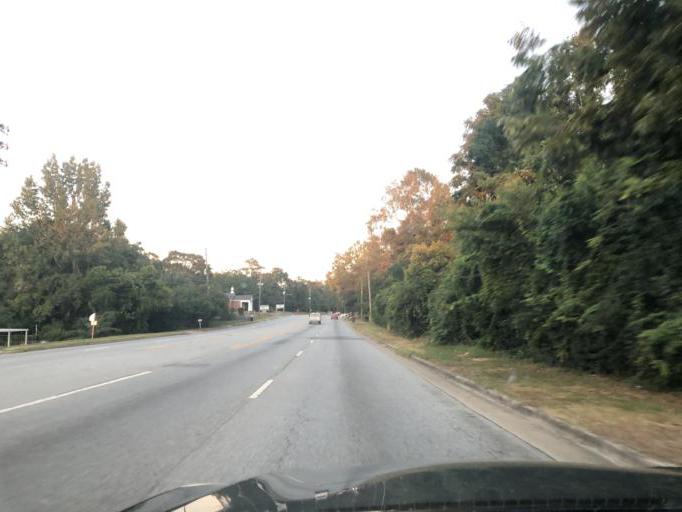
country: US
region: Georgia
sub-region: Muscogee County
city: Columbus
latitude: 32.4676
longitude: -84.9083
